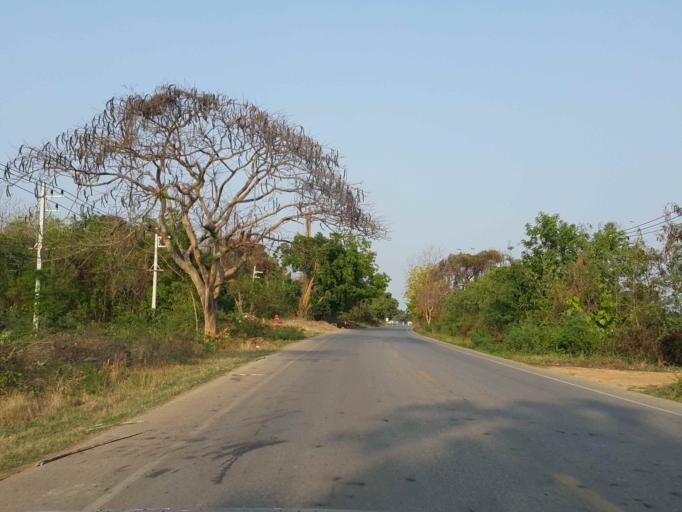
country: TH
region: Sukhothai
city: Sawankhalok
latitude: 17.3087
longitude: 99.7883
